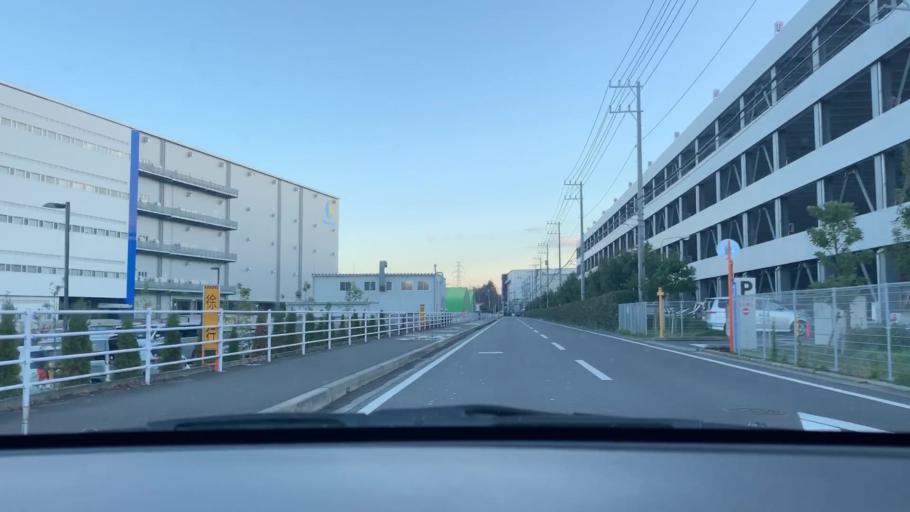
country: JP
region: Ibaraki
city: Moriya
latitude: 35.9097
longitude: 139.9446
